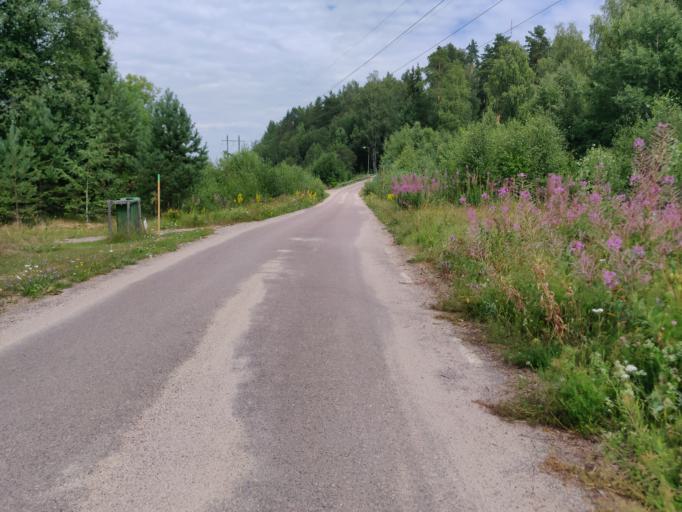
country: SE
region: Vaermland
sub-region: Munkfors Kommun
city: Munkfors
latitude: 59.9578
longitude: 13.5278
